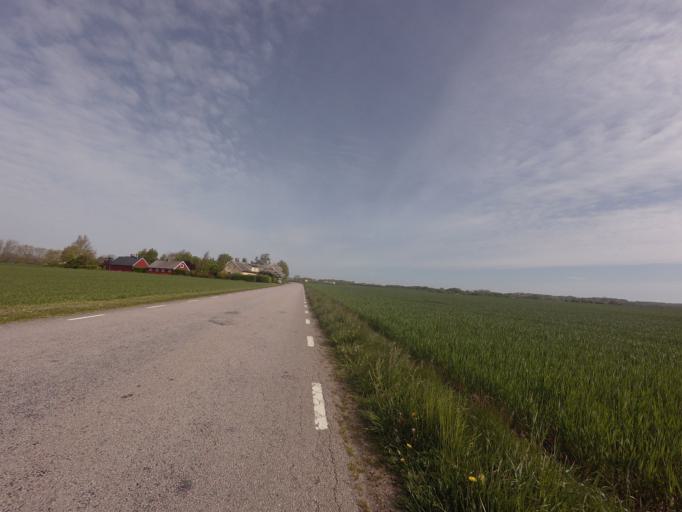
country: SE
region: Skane
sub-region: Hoganas Kommun
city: Hoganas
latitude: 56.2446
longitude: 12.5739
